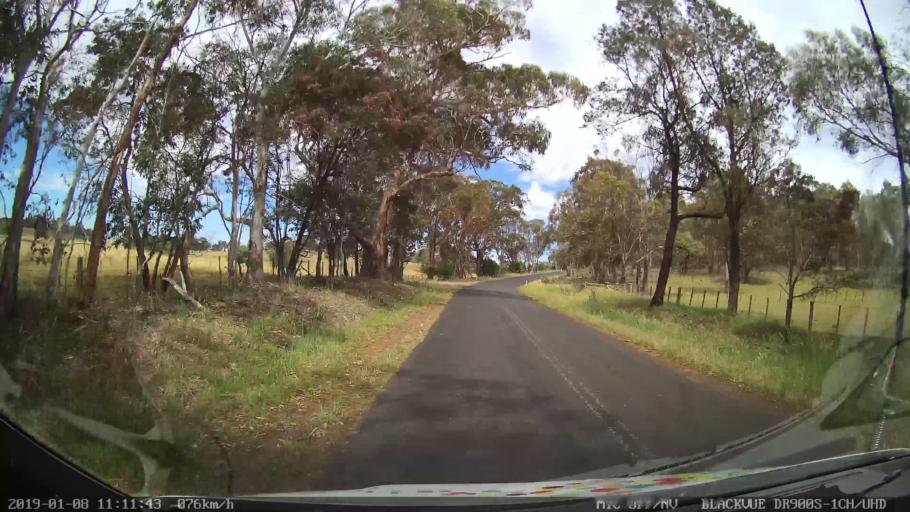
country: AU
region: New South Wales
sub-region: Guyra
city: Guyra
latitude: -30.2270
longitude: 151.6205
